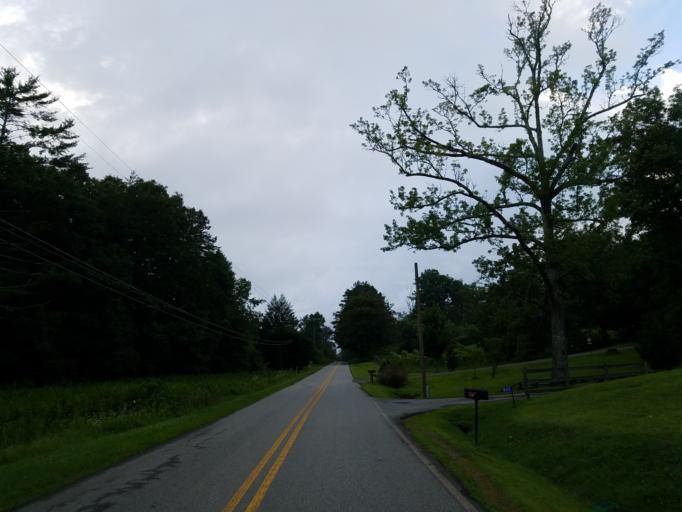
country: US
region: Georgia
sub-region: Fannin County
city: Blue Ridge
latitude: 34.8471
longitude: -84.3380
